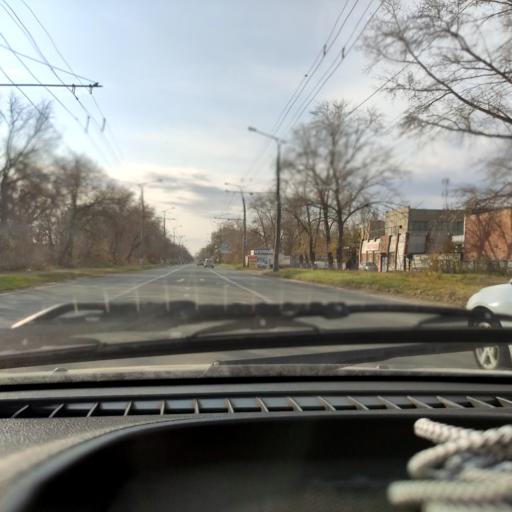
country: RU
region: Samara
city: Tol'yatti
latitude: 53.5303
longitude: 49.4378
